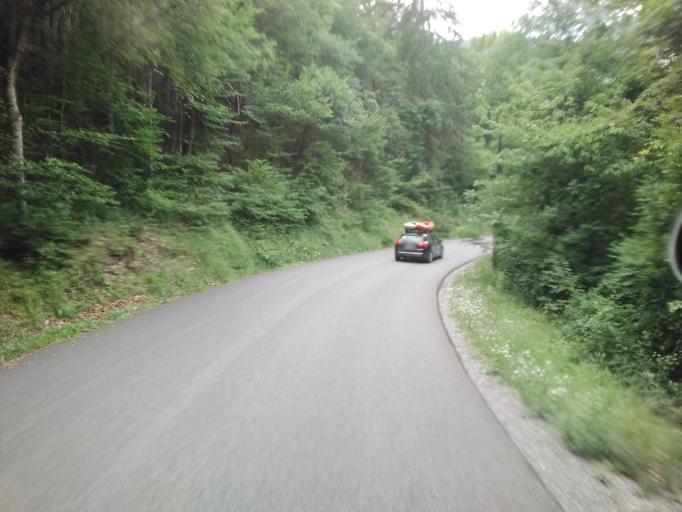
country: FR
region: Provence-Alpes-Cote d'Azur
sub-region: Departement des Alpes-de-Haute-Provence
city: Seyne-les-Alpes
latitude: 44.4493
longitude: 6.3944
